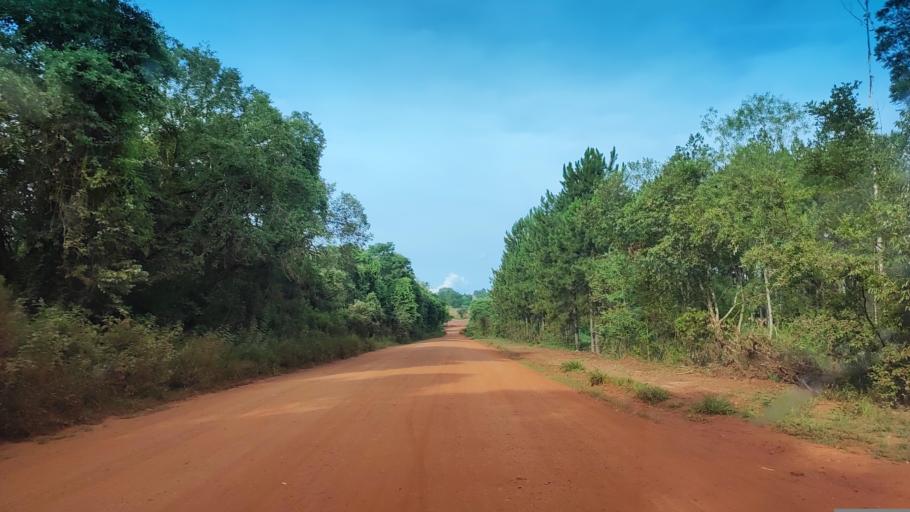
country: AR
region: Misiones
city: Gobernador Roca
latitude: -27.1389
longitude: -55.5212
